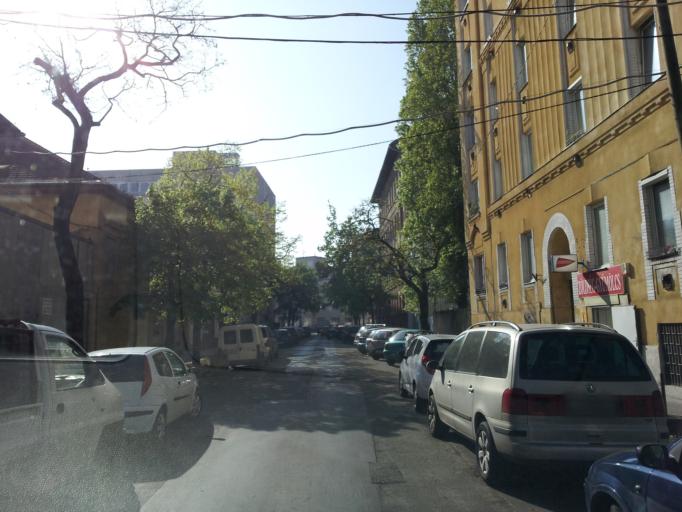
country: HU
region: Budapest
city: Budapest XIV. keruelet
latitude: 47.5029
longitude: 19.1146
